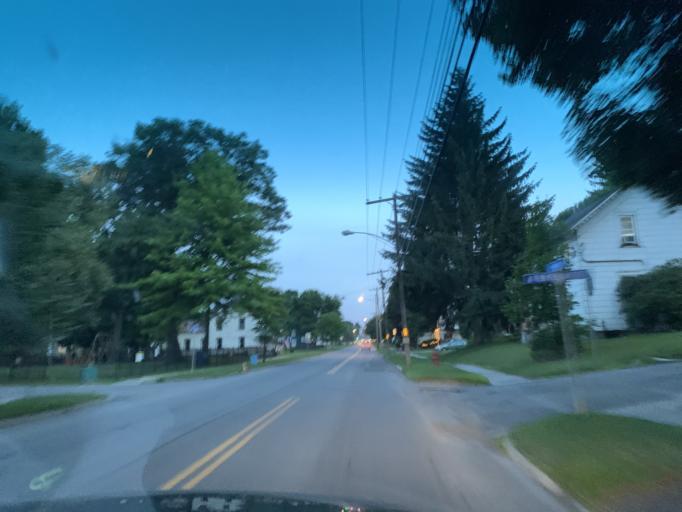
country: US
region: New York
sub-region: Chenango County
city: New Berlin
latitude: 42.6279
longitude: -75.3325
